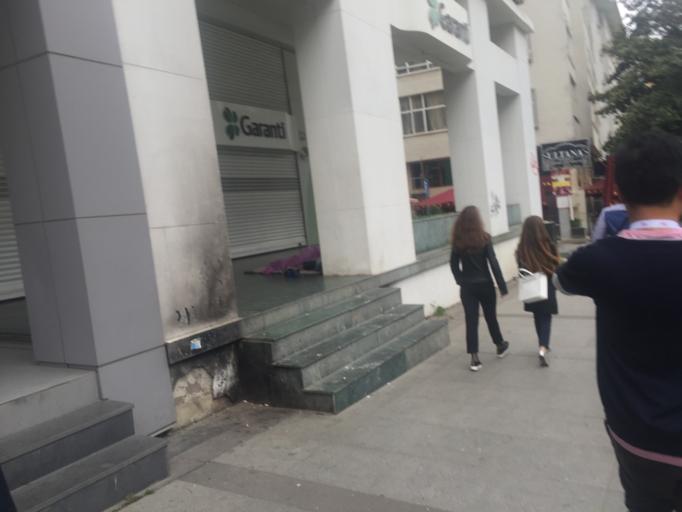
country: TR
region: Istanbul
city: Sisli
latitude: 41.0428
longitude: 28.9868
